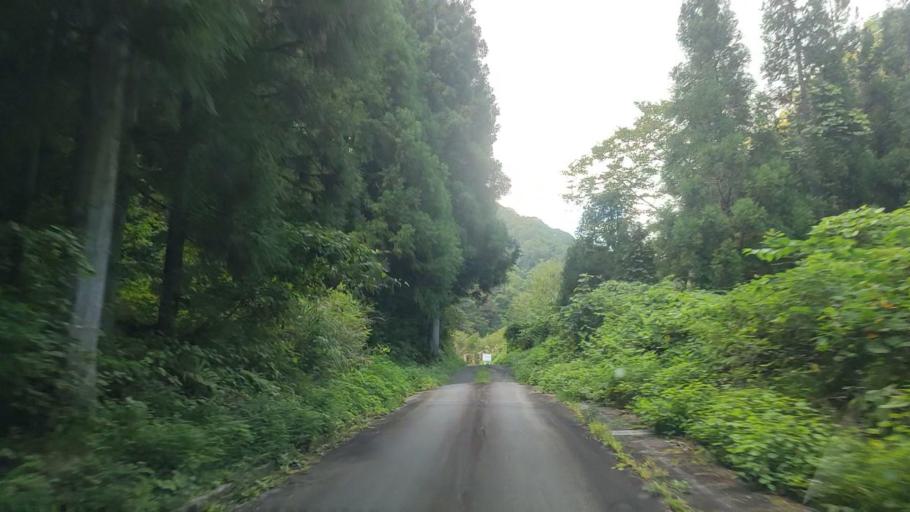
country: JP
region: Gifu
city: Takayama
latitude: 36.3136
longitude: 137.0860
